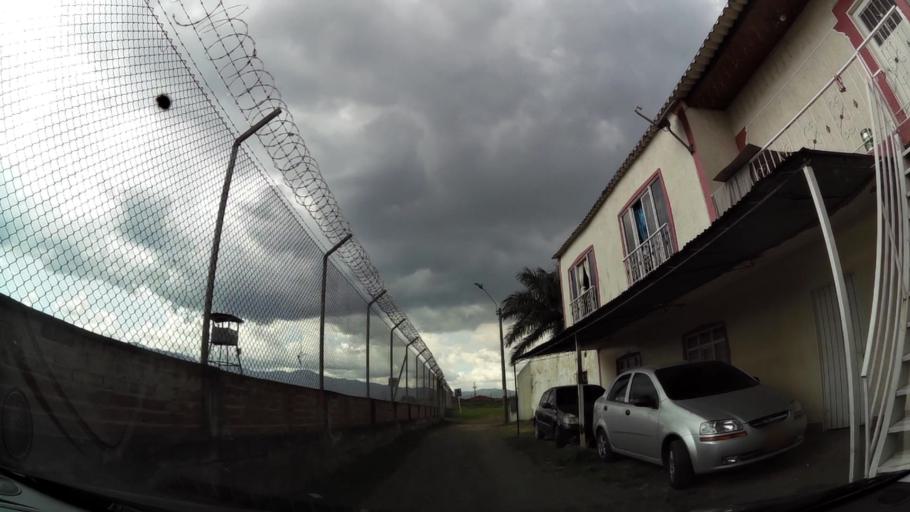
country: CO
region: Valle del Cauca
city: Cali
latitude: 3.4606
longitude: -76.4904
